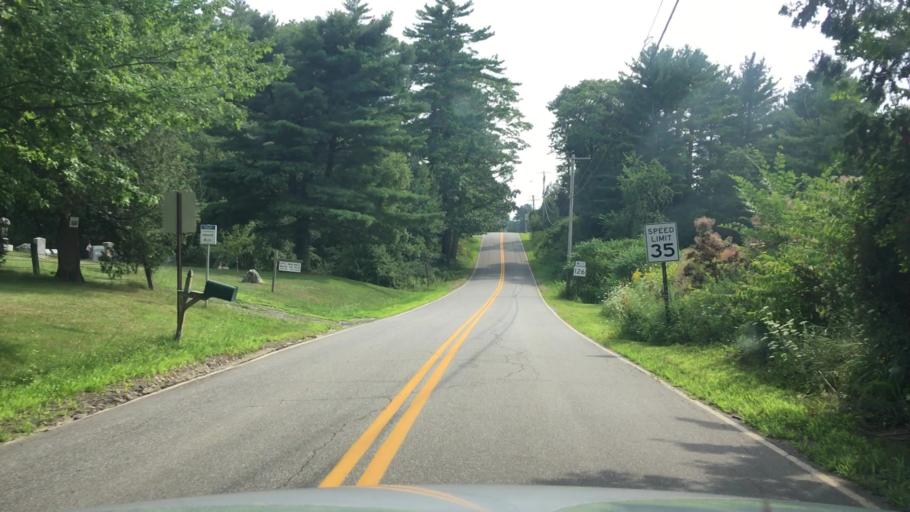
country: US
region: Maine
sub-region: Lincoln County
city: Jefferson
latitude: 44.2066
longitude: -69.4529
